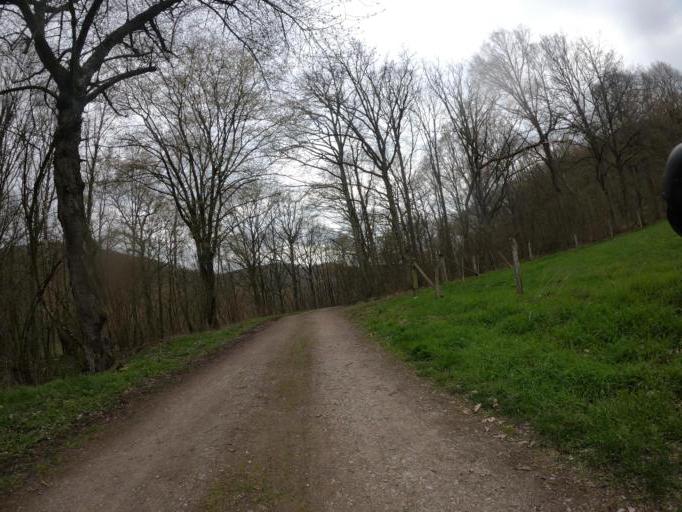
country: DE
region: North Rhine-Westphalia
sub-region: Regierungsbezirk Koln
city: Nideggen
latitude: 50.6804
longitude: 6.4287
